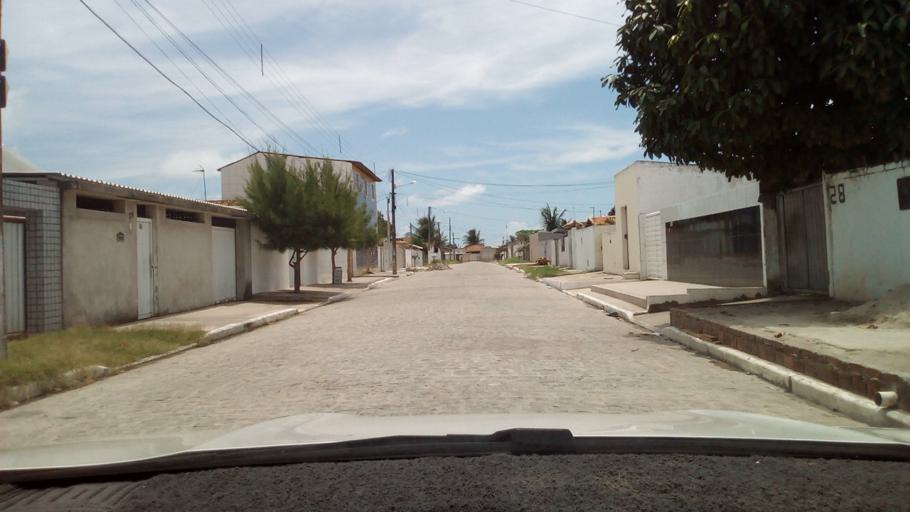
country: BR
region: Paraiba
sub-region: Joao Pessoa
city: Joao Pessoa
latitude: -7.1805
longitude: -34.8293
